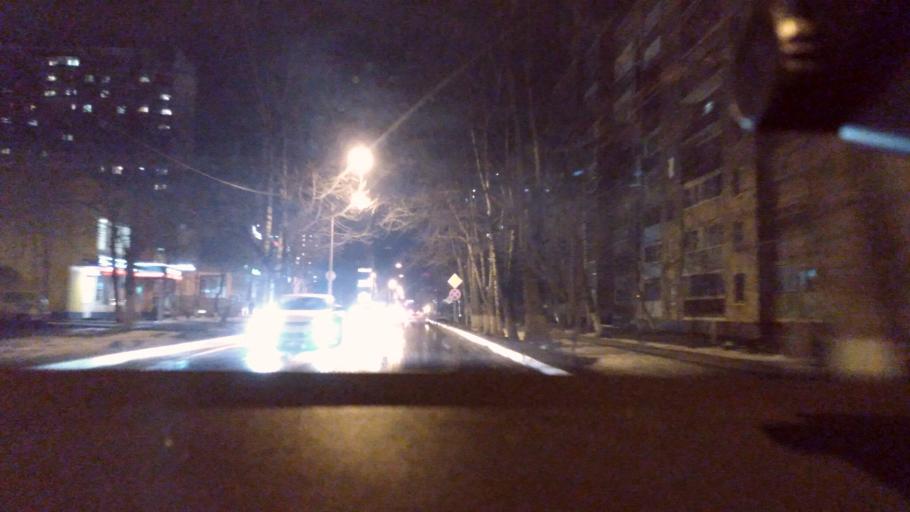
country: RU
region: Moskovskaya
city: Zheleznodorozhnyy
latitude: 55.7457
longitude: 37.9910
